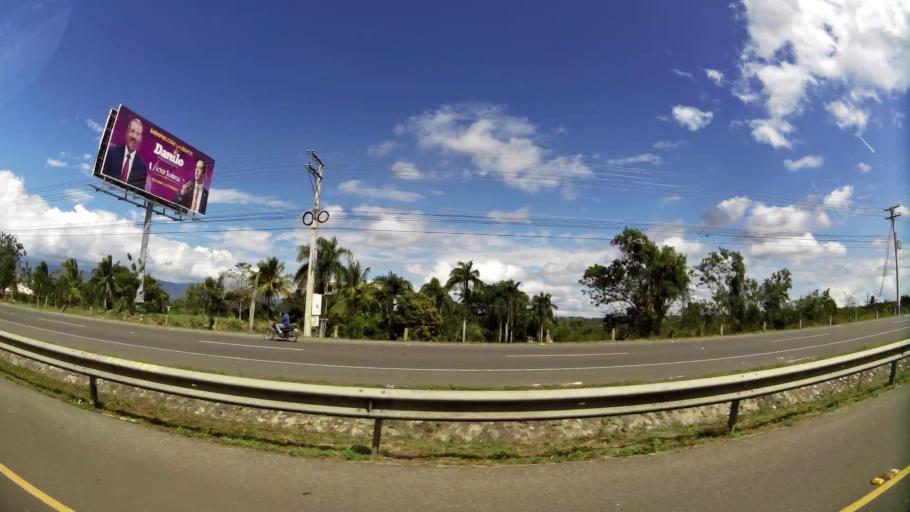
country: DO
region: Santiago
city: Licey al Medio
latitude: 19.3724
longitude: -70.6041
